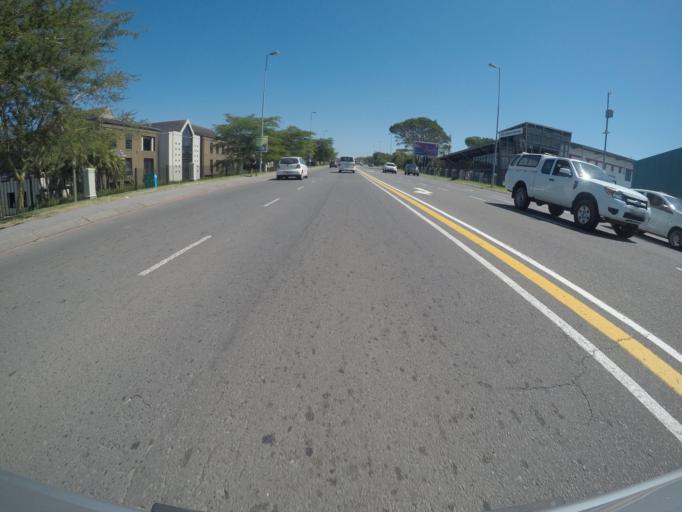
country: ZA
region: Eastern Cape
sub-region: Buffalo City Metropolitan Municipality
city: East London
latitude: -32.9568
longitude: 27.9346
